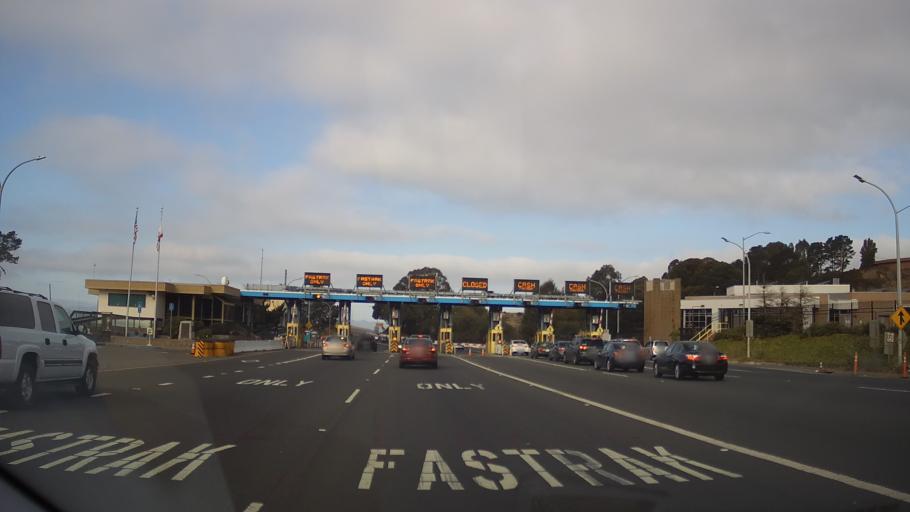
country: US
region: California
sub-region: Contra Costa County
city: North Richmond
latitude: 37.9323
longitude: -122.4024
